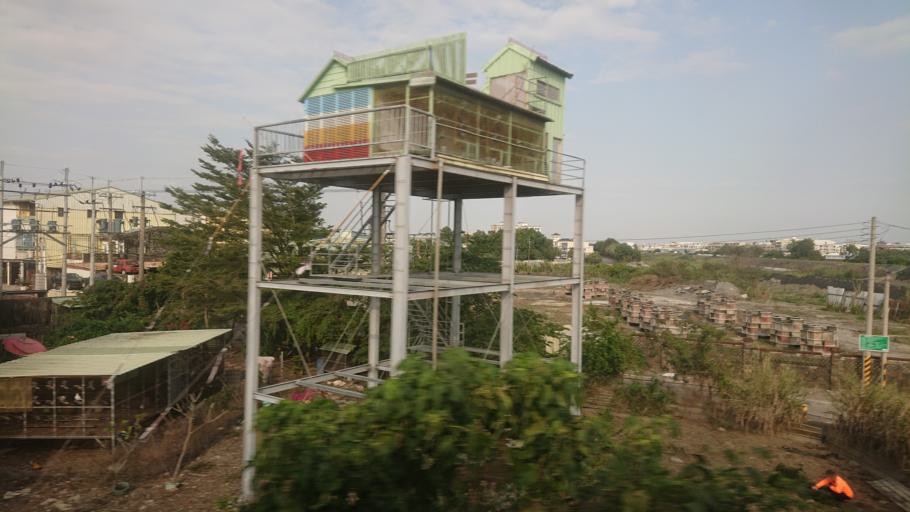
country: TW
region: Taiwan
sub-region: Yunlin
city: Douliu
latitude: 23.6802
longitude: 120.4872
